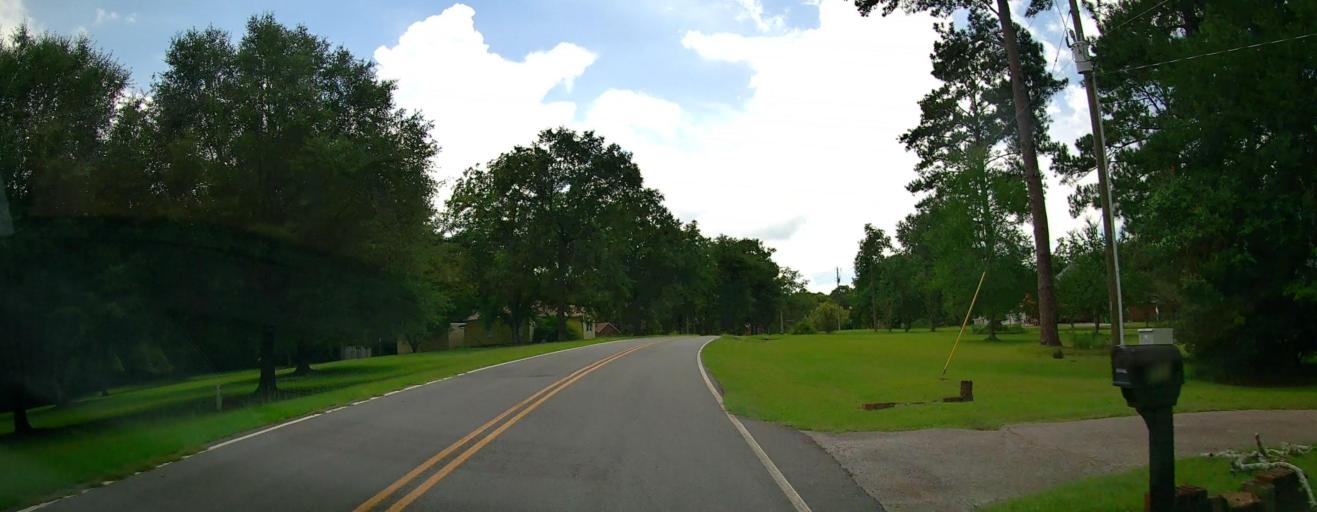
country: US
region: Georgia
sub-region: Houston County
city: Perry
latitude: 32.5175
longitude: -83.7200
